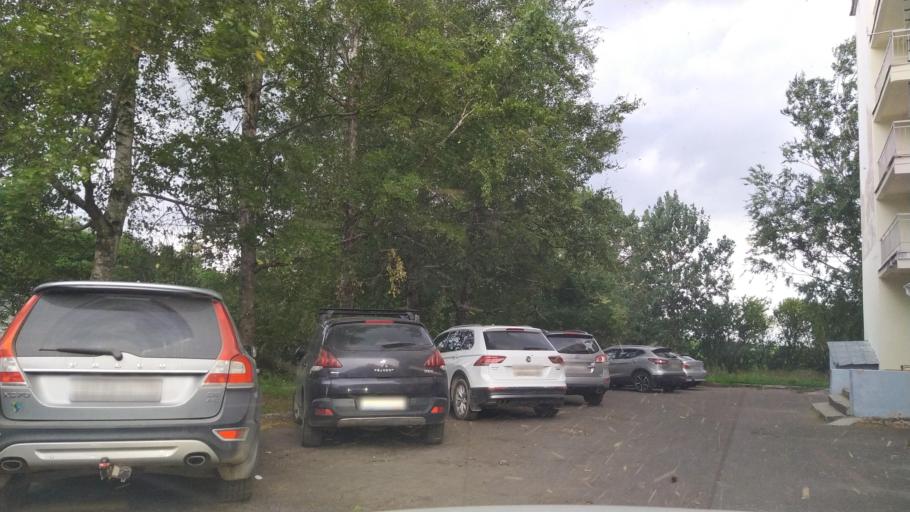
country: RU
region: Novgorod
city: Velikiy Novgorod
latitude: 58.5185
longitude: 31.2638
